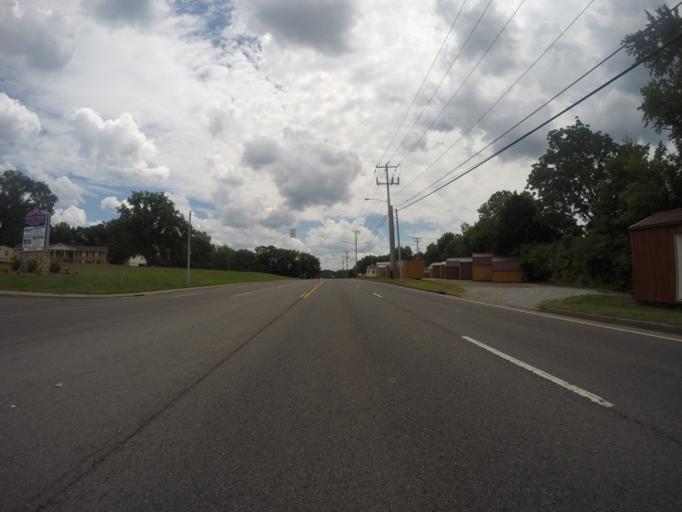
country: US
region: Tennessee
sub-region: Davidson County
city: Lakewood
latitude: 36.2361
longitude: -86.6273
